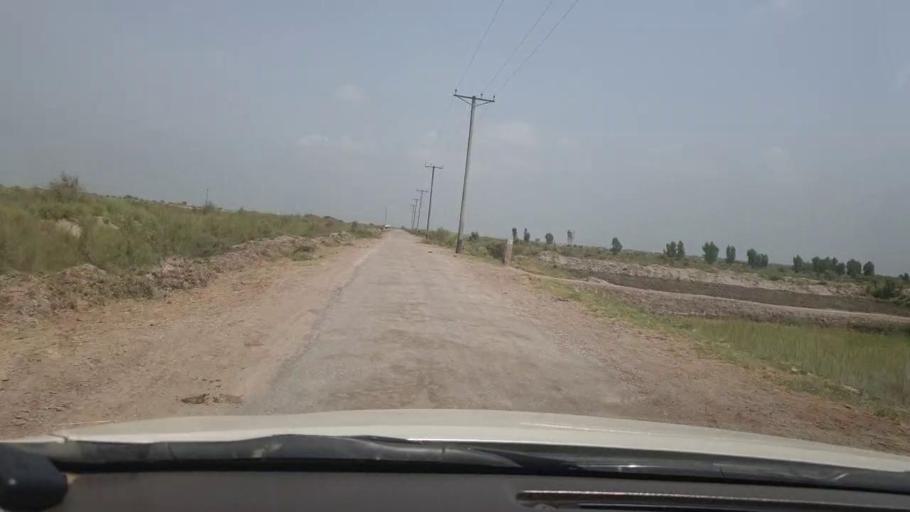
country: PK
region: Sindh
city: Garhi Yasin
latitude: 28.0048
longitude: 68.4999
